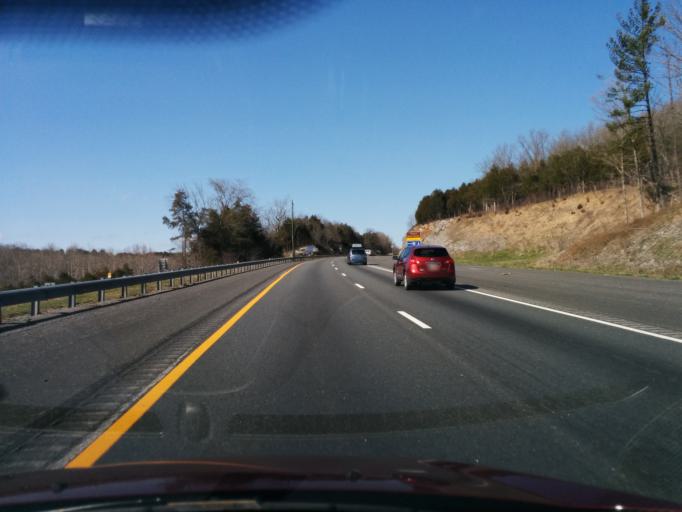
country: US
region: Virginia
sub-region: Rockbridge County
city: East Lexington
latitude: 37.7831
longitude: -79.4004
